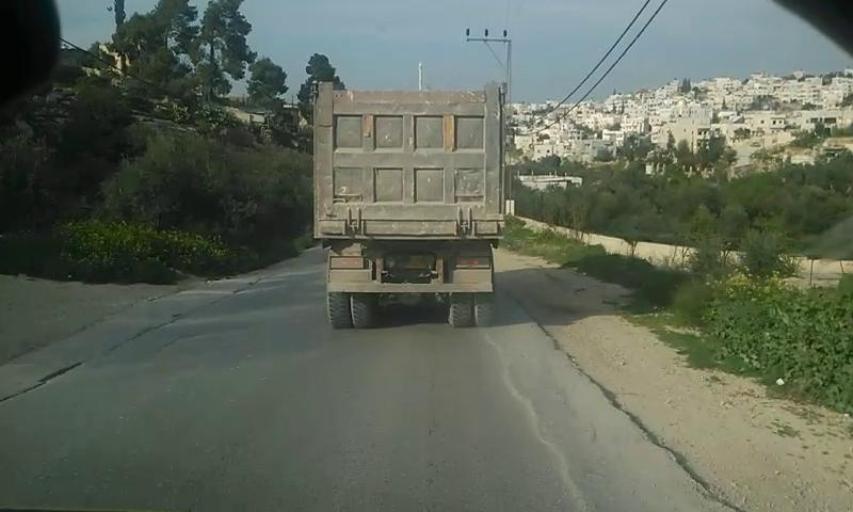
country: PS
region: West Bank
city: Bayt Ula
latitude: 31.5899
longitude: 35.0256
